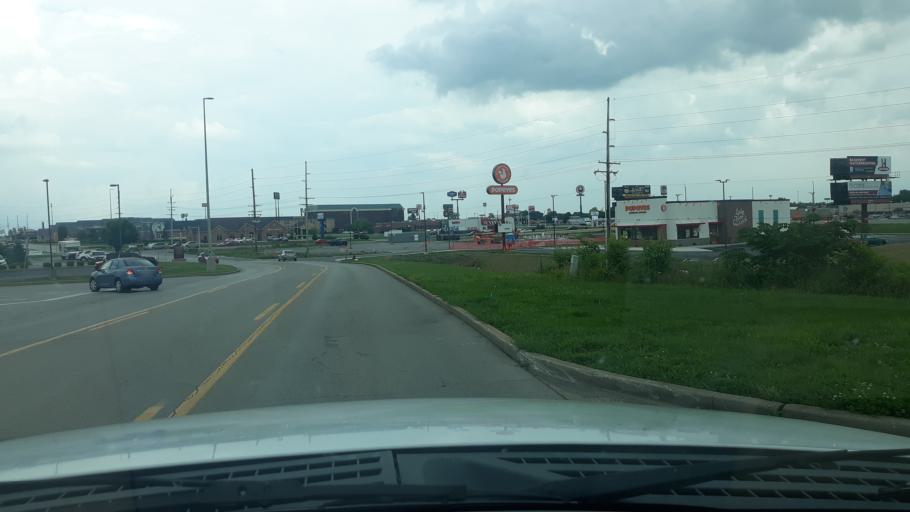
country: US
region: Illinois
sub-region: Williamson County
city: Marion
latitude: 37.7454
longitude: -88.9722
